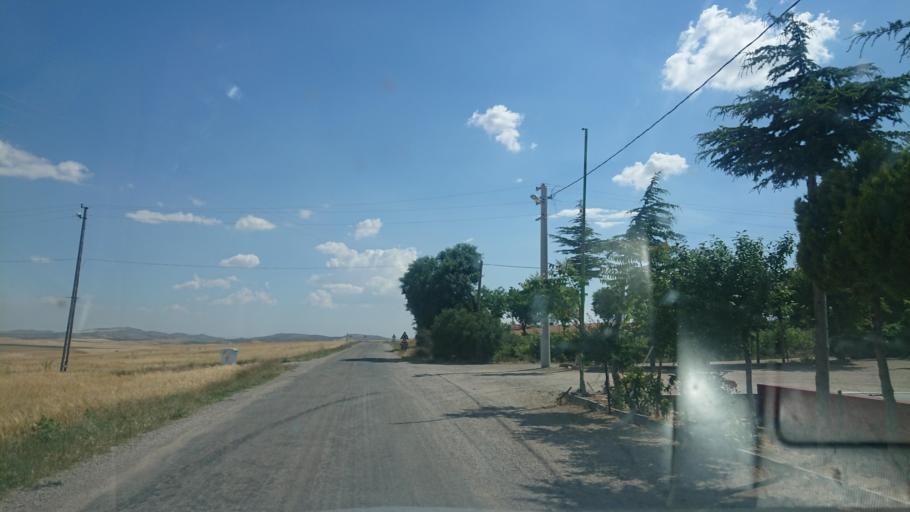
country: TR
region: Aksaray
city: Agacoren
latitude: 38.7574
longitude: 33.7813
